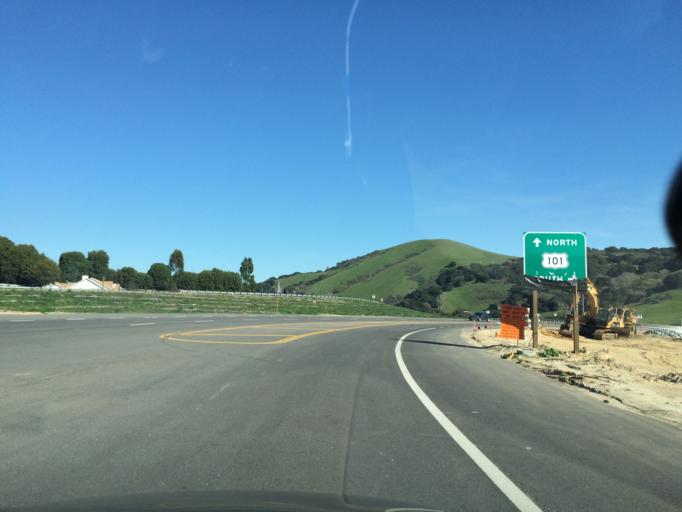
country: US
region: California
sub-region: San Benito County
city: Aromas
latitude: 36.8588
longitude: -121.6298
